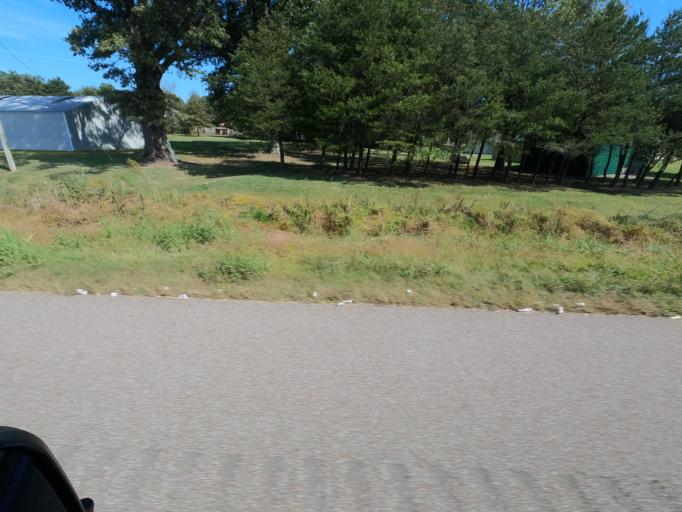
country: US
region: Tennessee
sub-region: Crockett County
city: Alamo
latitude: 35.8461
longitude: -89.1927
